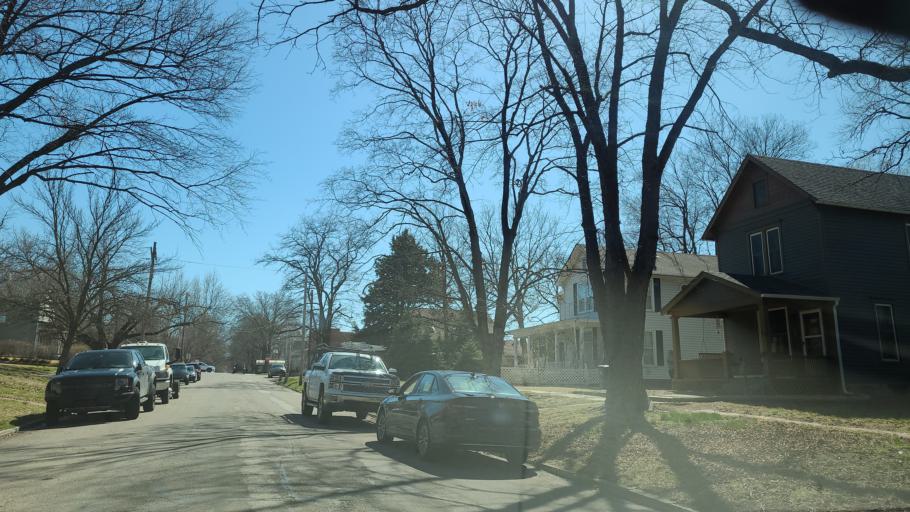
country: US
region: Kansas
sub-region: Douglas County
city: Lawrence
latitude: 38.9744
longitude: -95.2429
